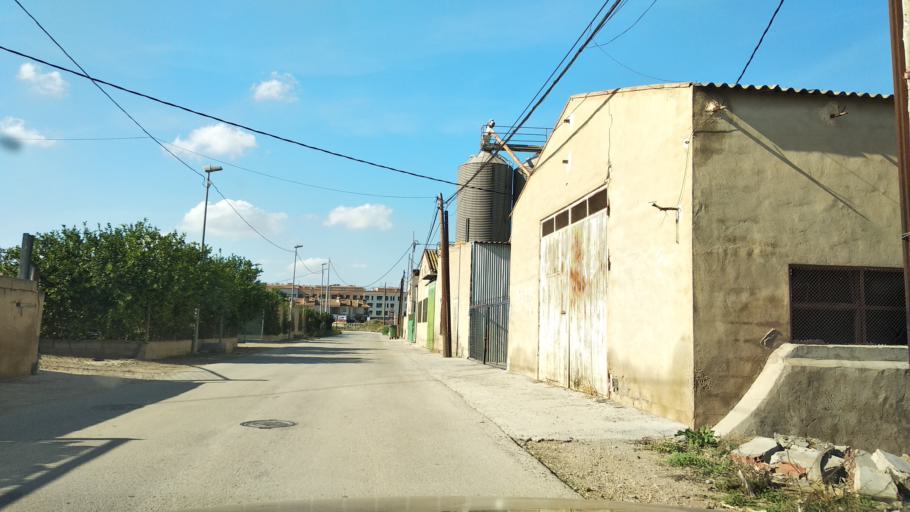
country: ES
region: Murcia
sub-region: Murcia
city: Santomera
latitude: 38.0569
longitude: -1.0438
